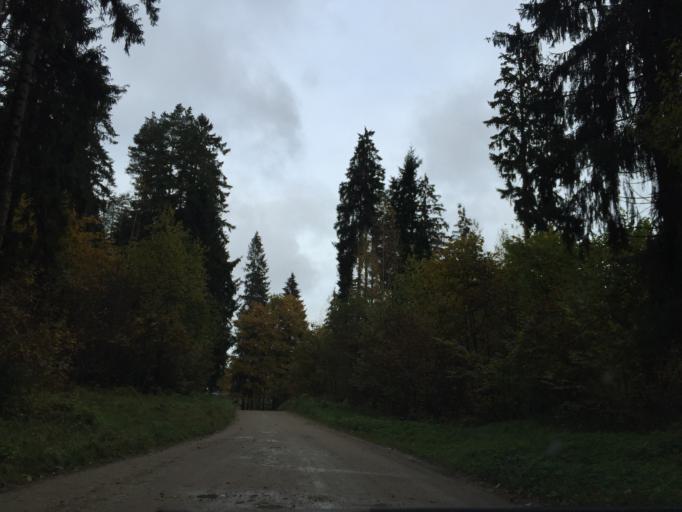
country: LV
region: Ogre
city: Ogre
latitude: 56.8071
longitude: 24.6330
